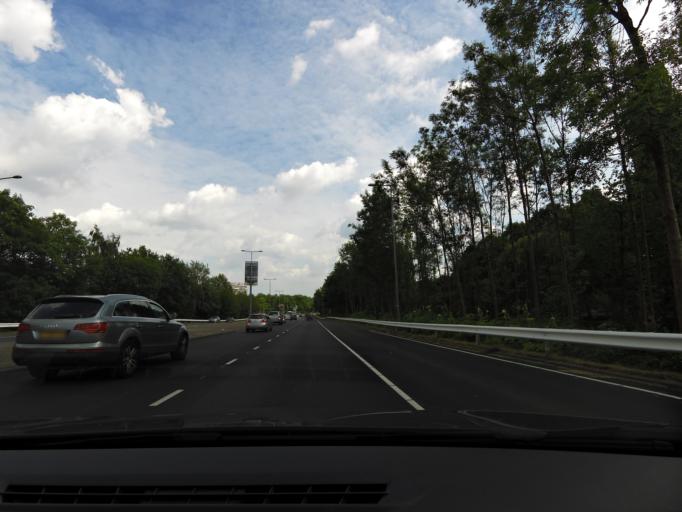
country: NL
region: South Holland
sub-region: Gemeente Barendrecht
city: Barendrecht
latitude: 51.8766
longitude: 4.5078
